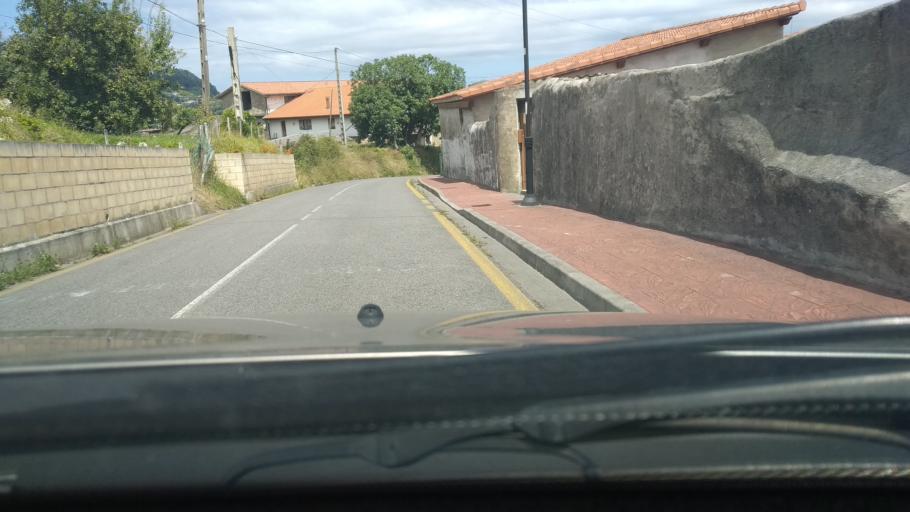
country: ES
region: Basque Country
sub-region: Bizkaia
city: Bermeo
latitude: 43.4127
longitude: -2.7318
